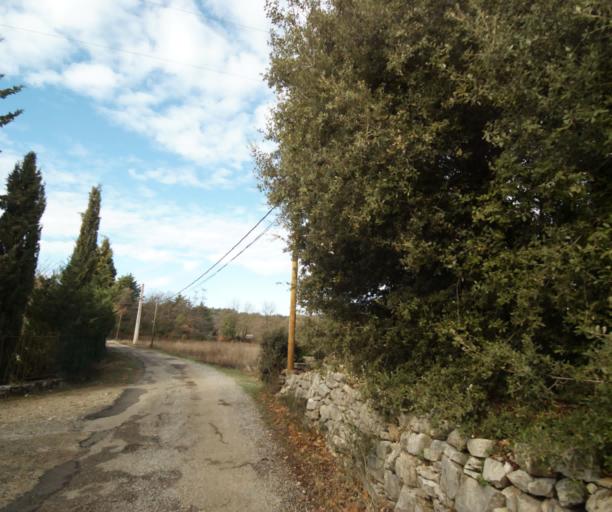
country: FR
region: Provence-Alpes-Cote d'Azur
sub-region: Departement du Var
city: Trans-en-Provence
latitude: 43.5061
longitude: 6.4746
